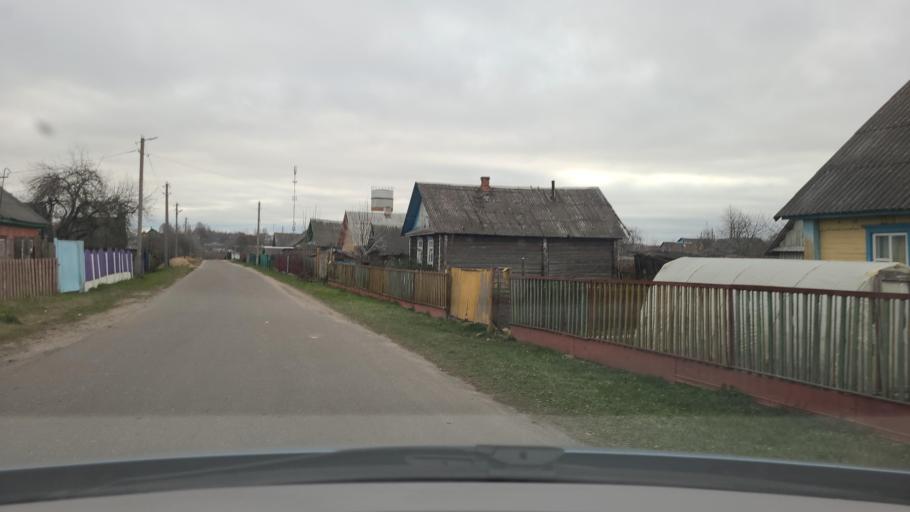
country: BY
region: Minsk
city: Khalopyenichy
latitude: 54.5174
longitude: 28.9550
